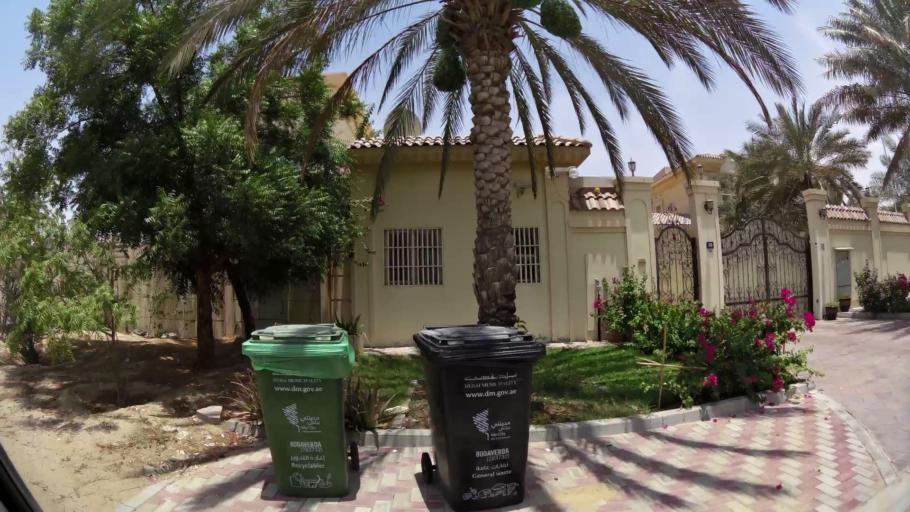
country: AE
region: Ash Shariqah
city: Sharjah
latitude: 25.2405
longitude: 55.4573
